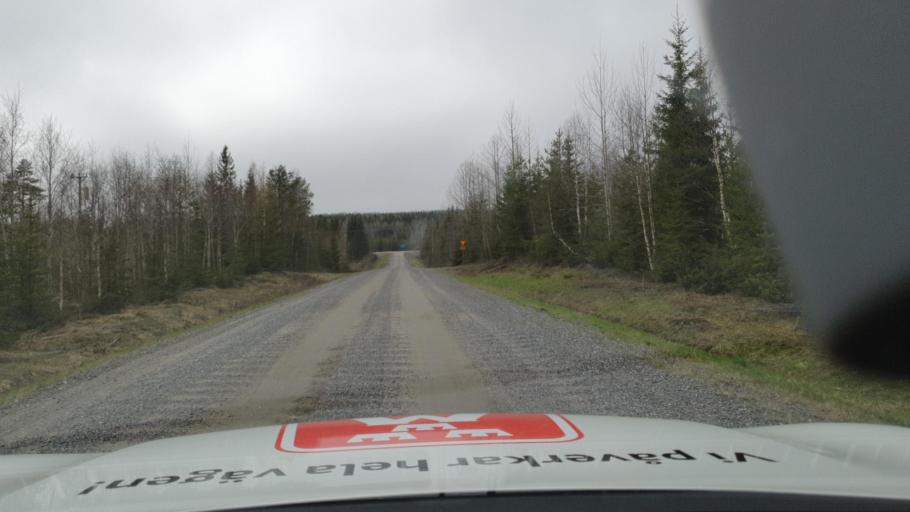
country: SE
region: Vaesterbotten
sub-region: Bjurholms Kommun
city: Bjurholm
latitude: 63.7896
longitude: 19.3112
